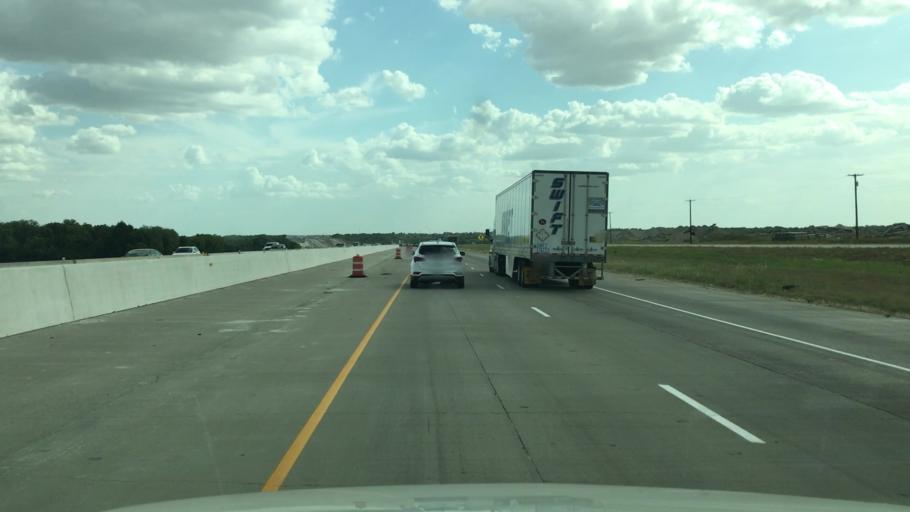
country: US
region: Texas
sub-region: McLennan County
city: Bruceville-Eddy
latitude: 31.2773
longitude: -97.2617
